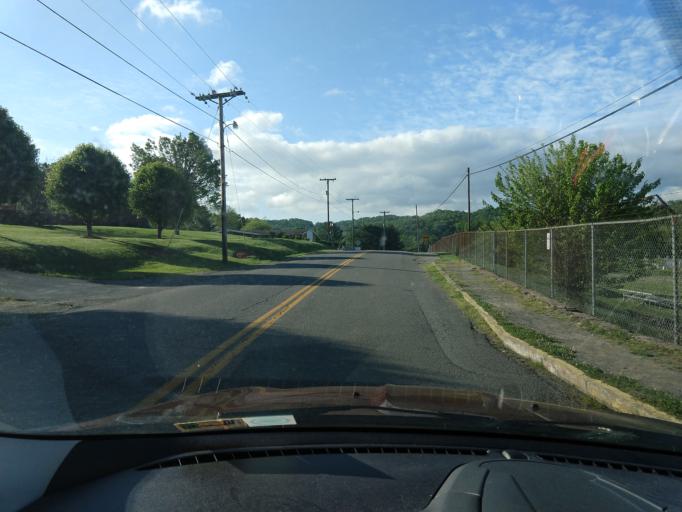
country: US
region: Virginia
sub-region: City of Galax
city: Galax
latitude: 36.7122
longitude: -80.9702
